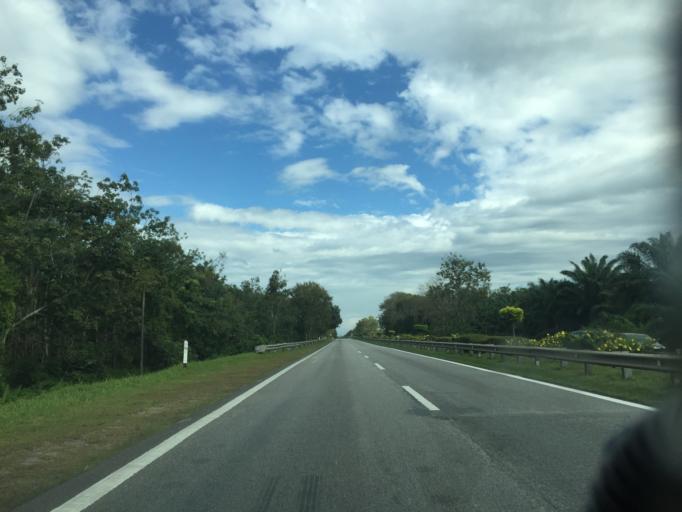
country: MY
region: Kedah
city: Jitra
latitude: 6.3816
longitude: 100.4246
